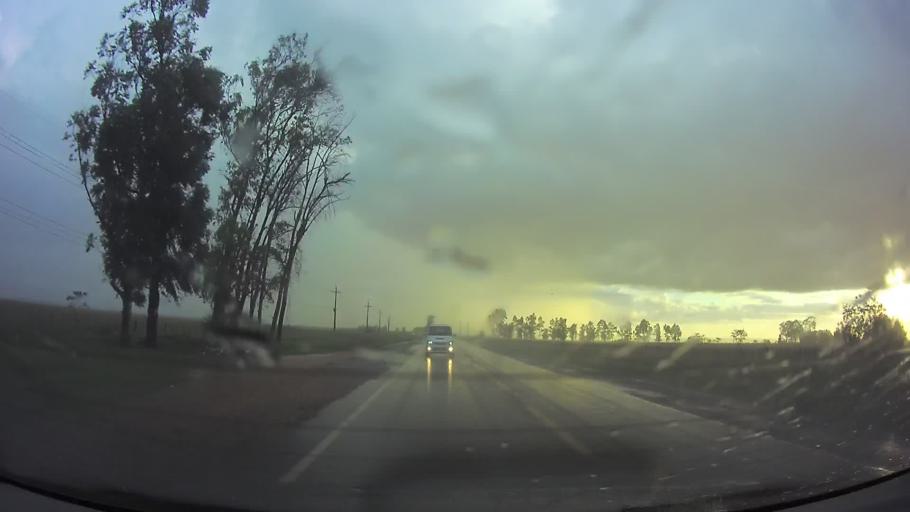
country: PY
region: Paraguari
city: Paraguari
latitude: -25.6487
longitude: -57.1591
